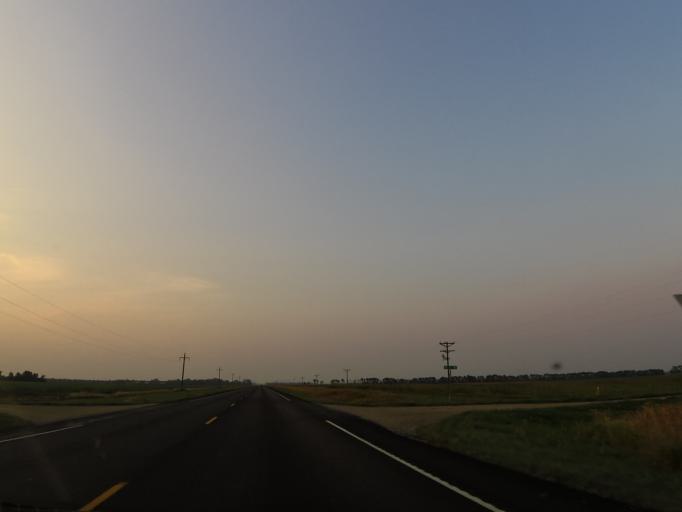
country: US
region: North Dakota
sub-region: Walsh County
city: Park River
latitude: 48.2524
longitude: -97.6225
